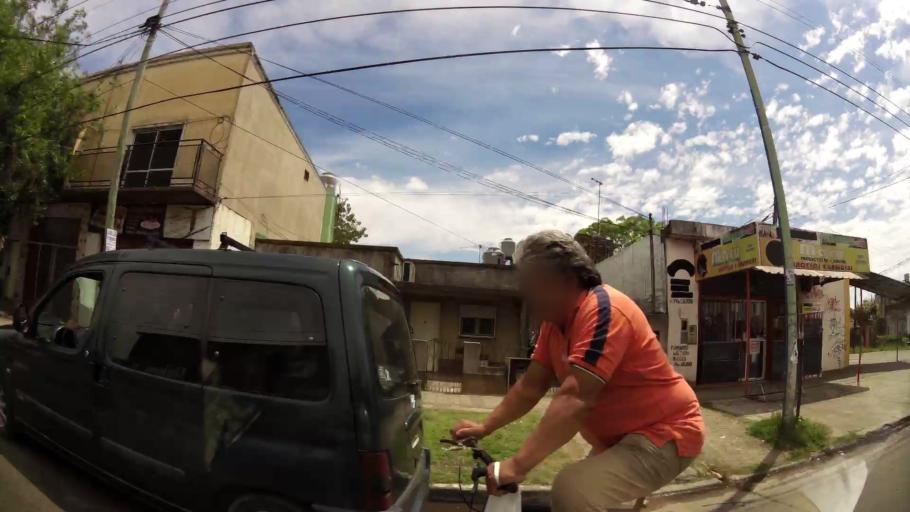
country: AR
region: Buenos Aires
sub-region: Partido de Quilmes
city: Quilmes
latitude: -34.7697
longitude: -58.2419
